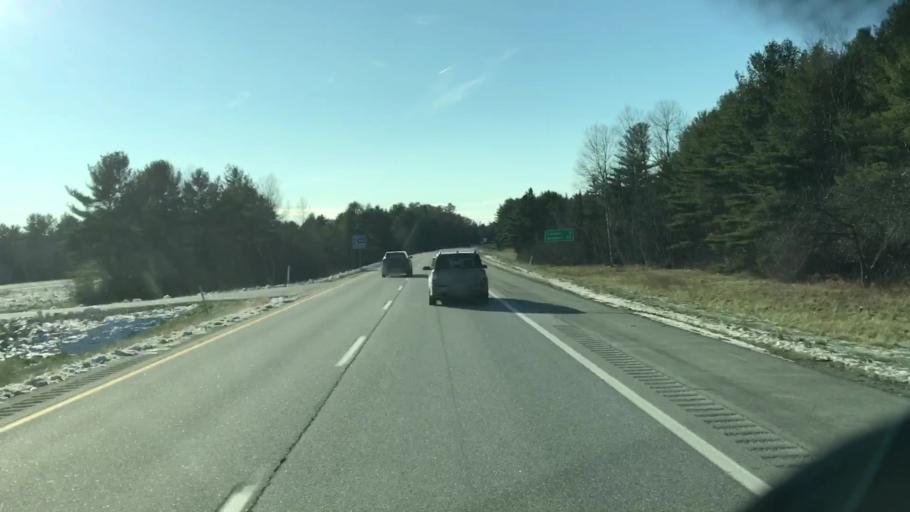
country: US
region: Maine
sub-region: Penobscot County
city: Hampden
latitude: 44.7695
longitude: -68.8737
